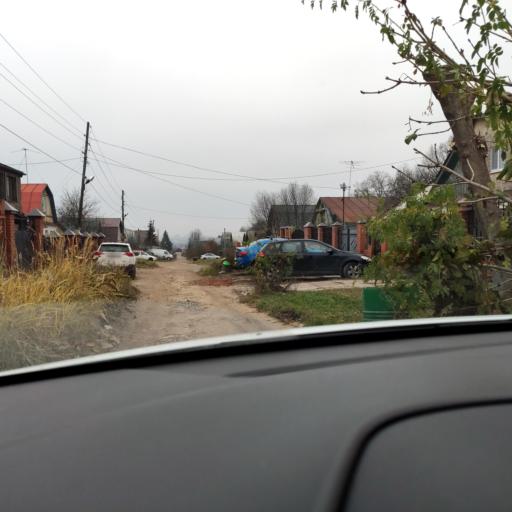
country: RU
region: Tatarstan
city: Vysokaya Gora
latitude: 55.8504
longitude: 49.2197
